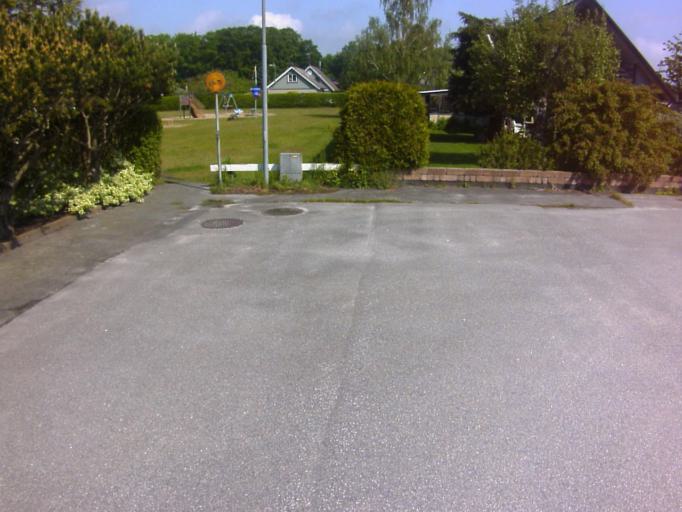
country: SE
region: Blekinge
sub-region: Solvesborgs Kommun
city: Soelvesborg
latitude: 56.0392
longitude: 14.5634
